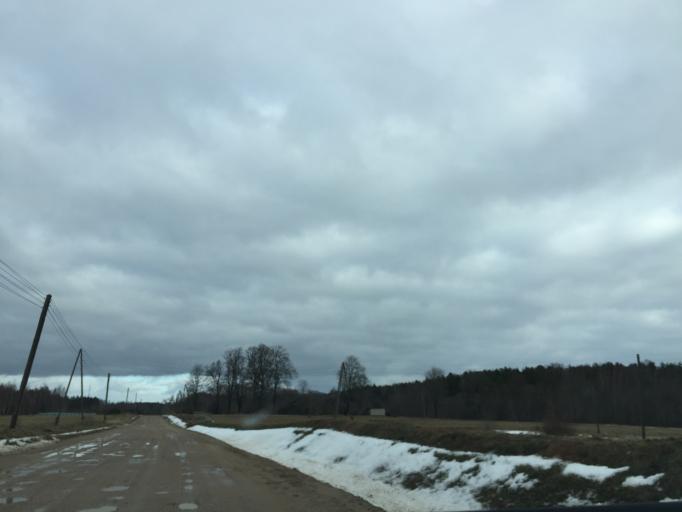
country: LV
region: Salacgrivas
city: Ainazi
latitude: 57.8504
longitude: 24.4868
